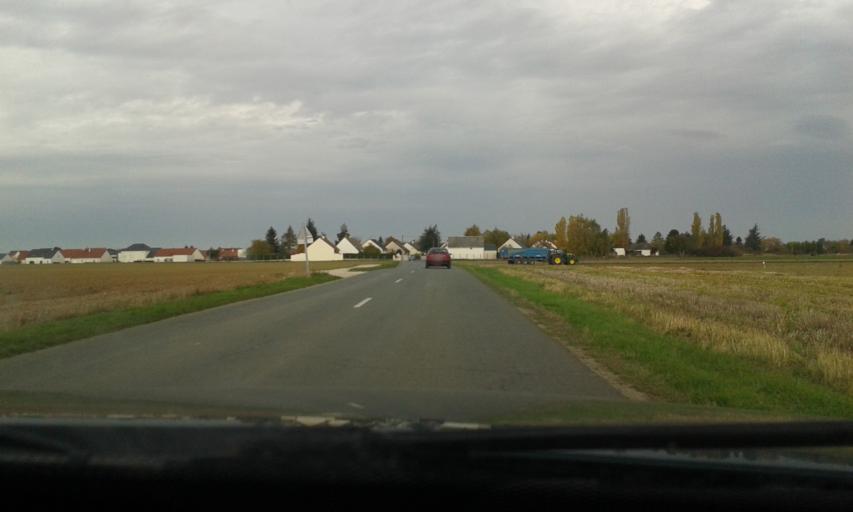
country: FR
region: Centre
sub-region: Departement du Loiret
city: Gidy
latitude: 47.9786
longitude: 1.8414
